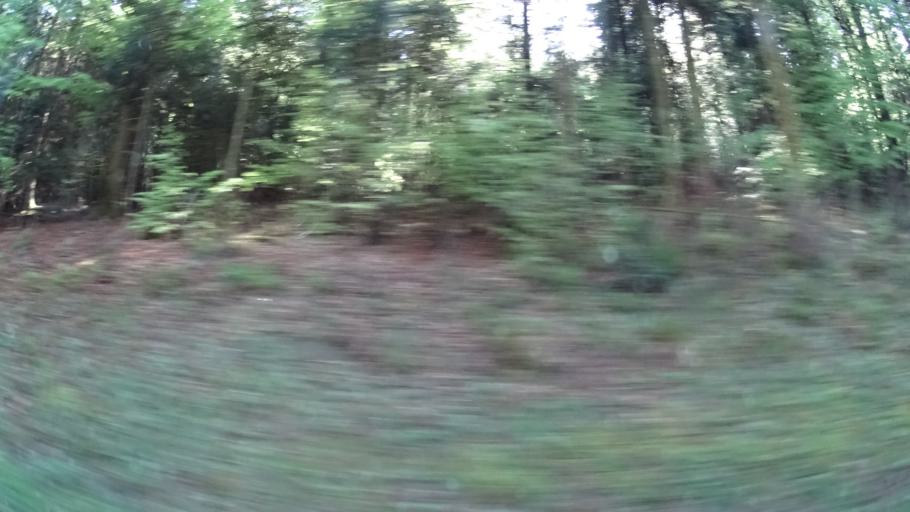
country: DE
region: Baden-Wuerttemberg
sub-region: Karlsruhe Region
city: Bad Wildbad
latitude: 48.7332
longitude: 8.5746
